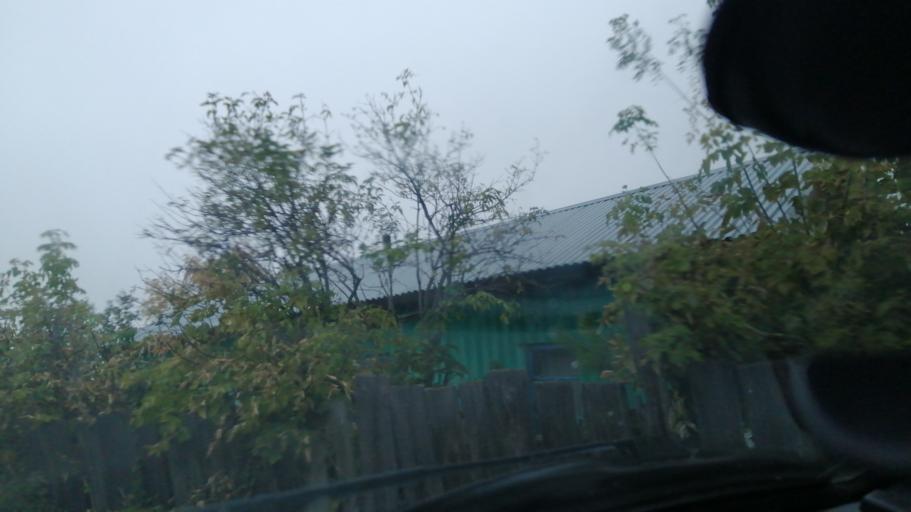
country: RU
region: Novosibirsk
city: Krasnozerskoye
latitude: 53.9734
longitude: 79.2478
